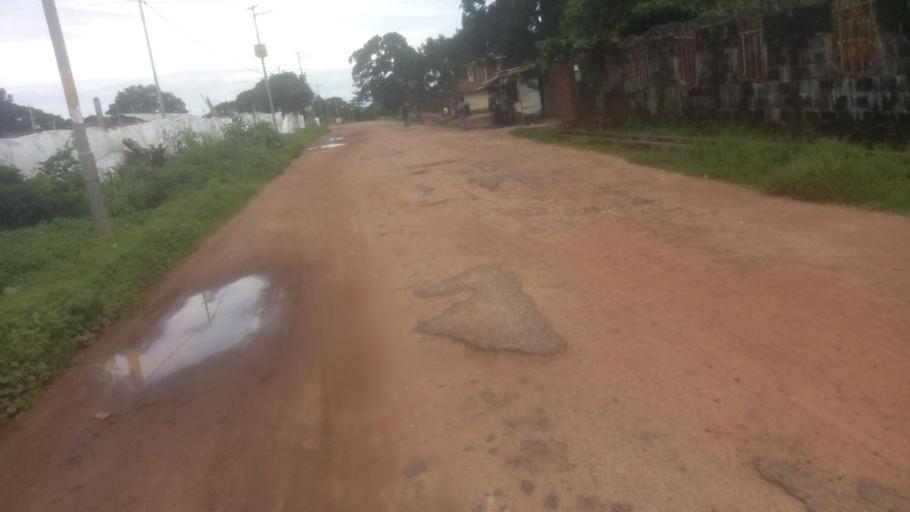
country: SL
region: Northern Province
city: Masoyila
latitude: 8.6019
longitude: -13.1977
